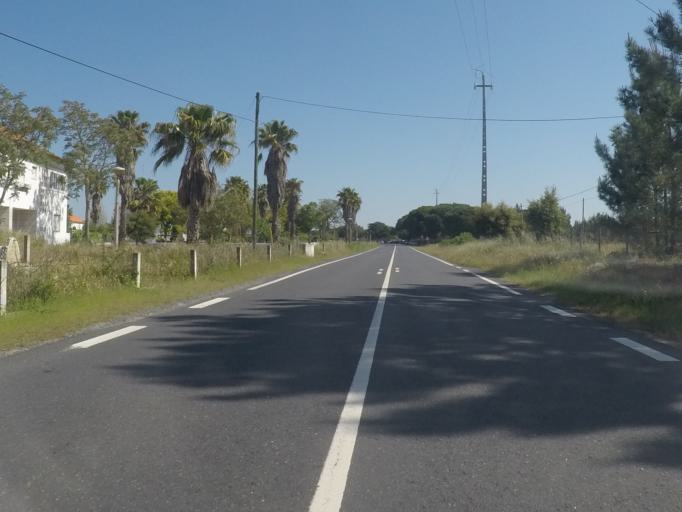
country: PT
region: Setubal
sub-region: Grandola
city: Grandola
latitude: 38.2664
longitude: -8.7284
